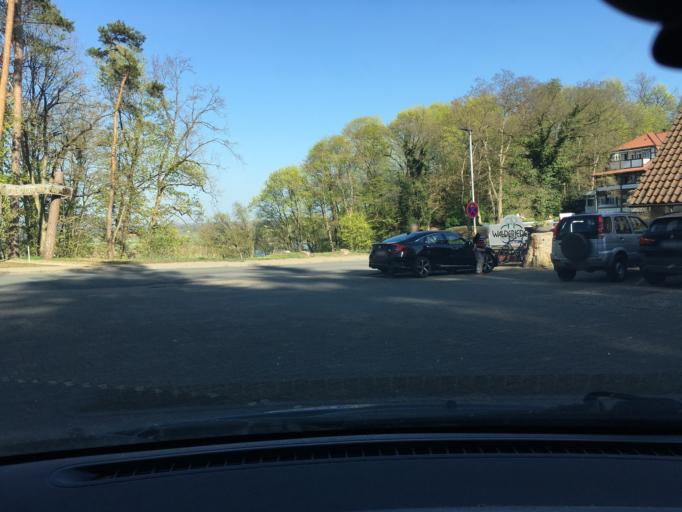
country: DE
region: Lower Saxony
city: Hitzacker
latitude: 53.1549
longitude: 11.0407
